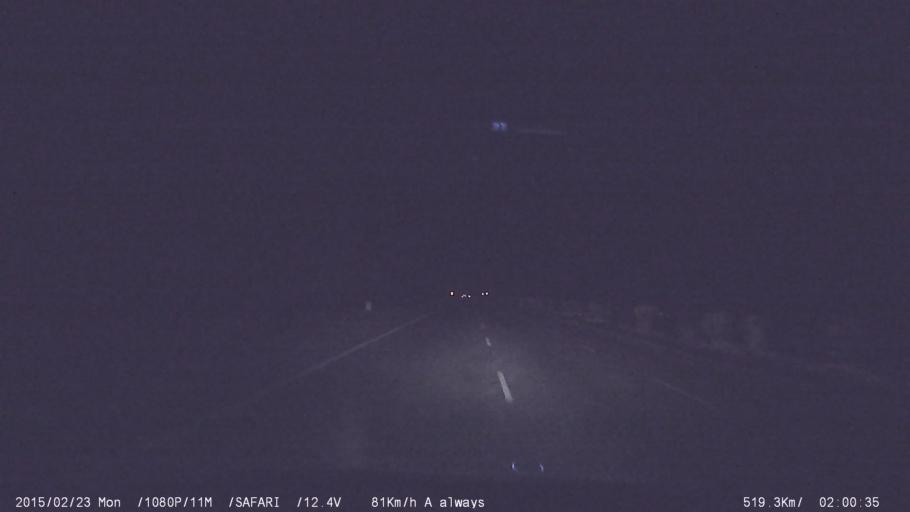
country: IN
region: Tamil Nadu
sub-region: Krishnagiri
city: Krishnagiri
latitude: 12.6244
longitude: 78.0807
